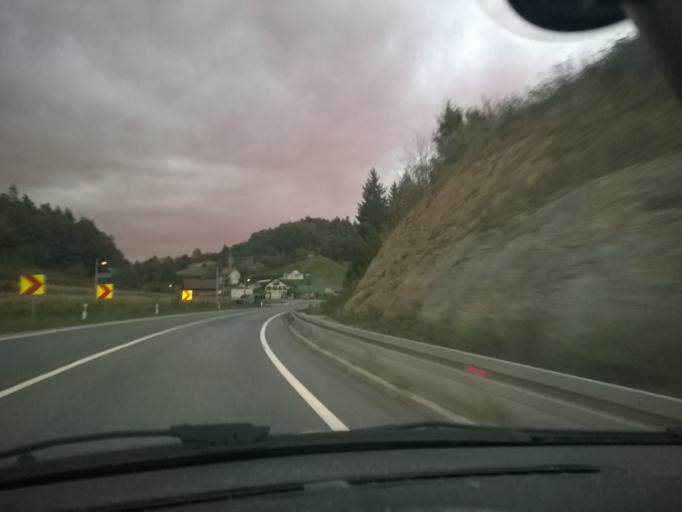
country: SI
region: Zetale
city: Zetale
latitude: 46.2560
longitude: 15.8580
